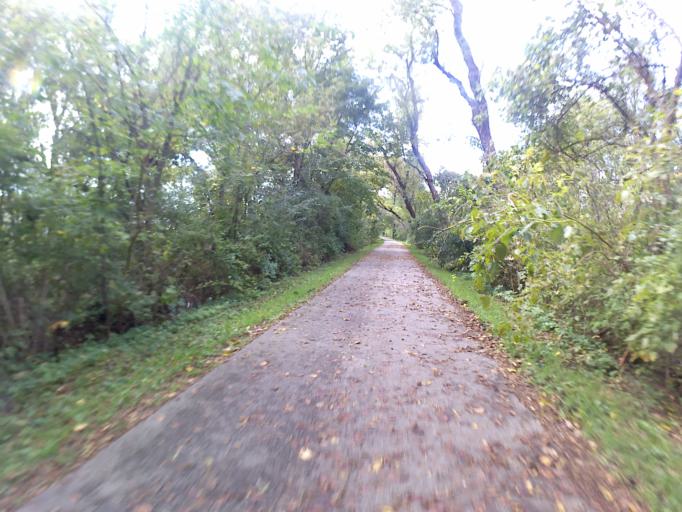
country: US
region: Illinois
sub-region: Kane County
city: Batavia
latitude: 41.8323
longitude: -88.2916
